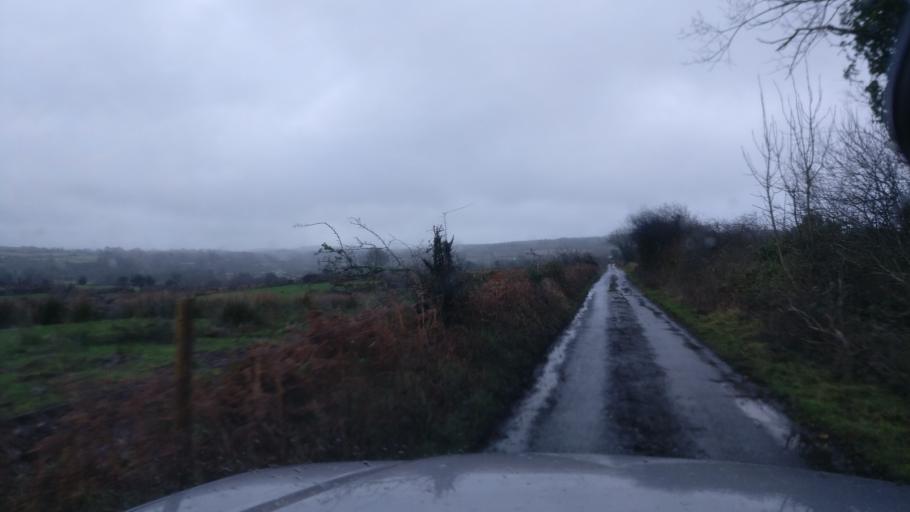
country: IE
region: Connaught
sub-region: County Galway
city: Loughrea
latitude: 53.1524
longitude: -8.6330
